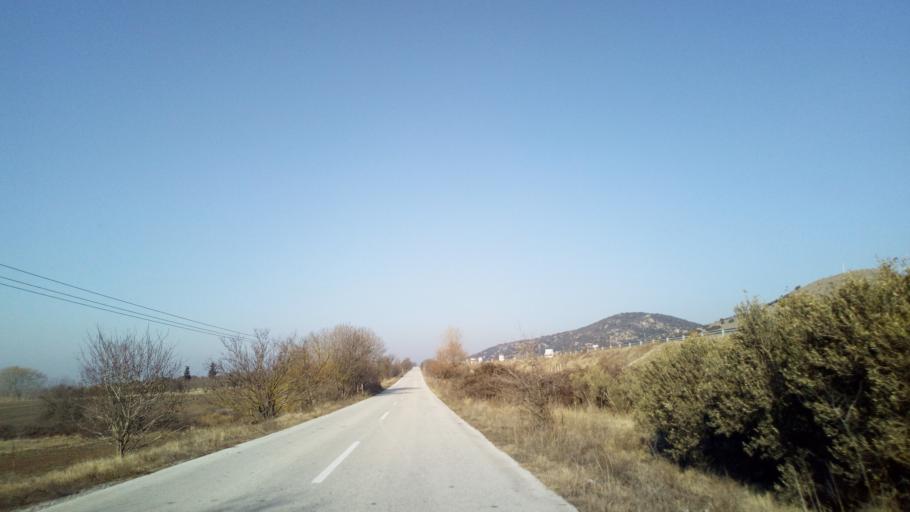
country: GR
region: Central Macedonia
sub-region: Nomos Thessalonikis
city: Gerakarou
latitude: 40.7004
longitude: 23.2030
